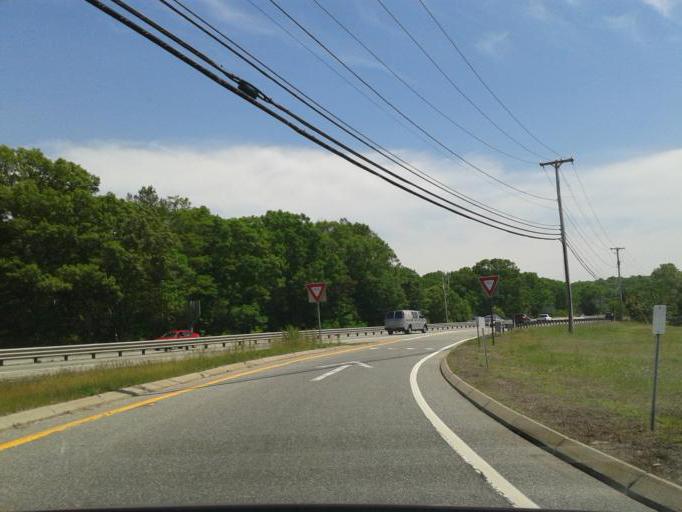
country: US
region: Rhode Island
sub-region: Washington County
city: North Kingstown
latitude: 41.5318
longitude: -71.4675
